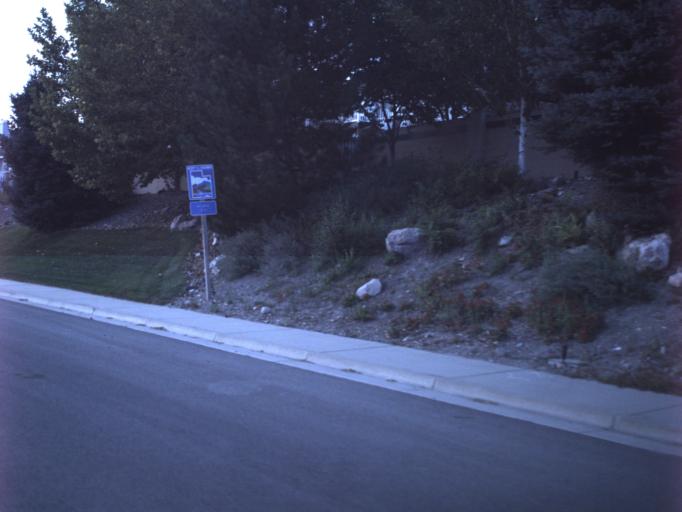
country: US
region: Utah
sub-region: Utah County
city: Springville
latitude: 40.2011
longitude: -111.6208
